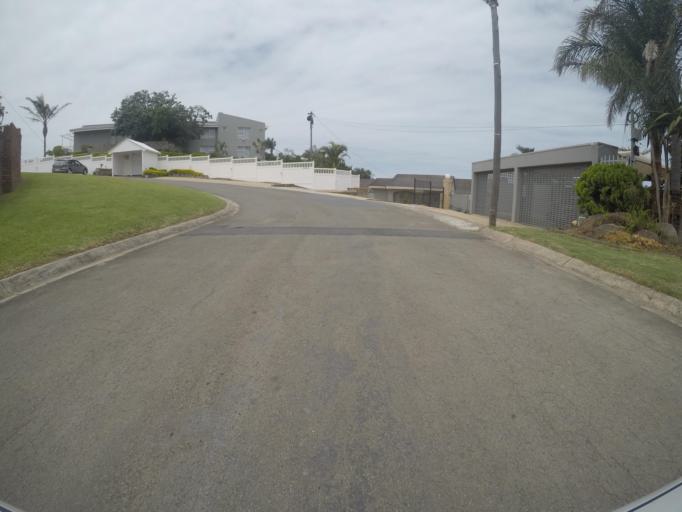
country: ZA
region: Eastern Cape
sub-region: Buffalo City Metropolitan Municipality
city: East London
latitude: -32.9789
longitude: 27.9454
